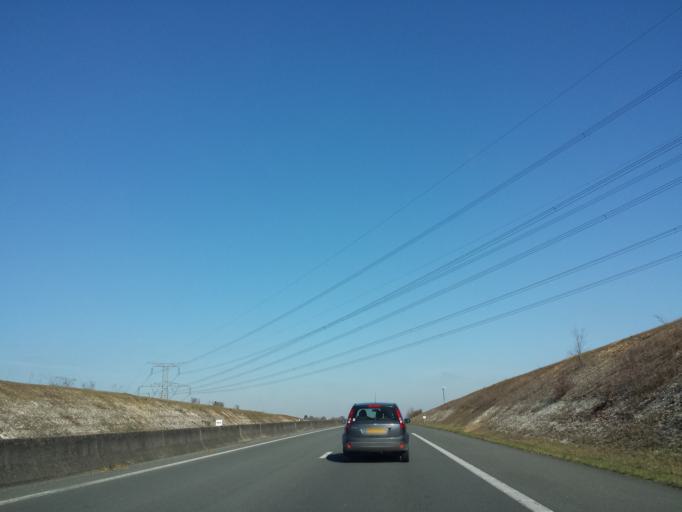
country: FR
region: Picardie
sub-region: Departement de la Somme
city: Saleux
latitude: 49.8102
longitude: 2.2435
